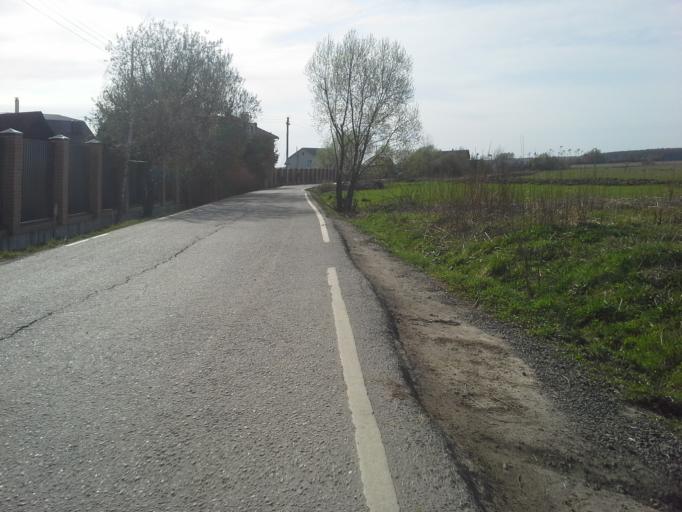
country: RU
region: Moskovskaya
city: Vatutinki
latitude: 55.4603
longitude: 37.3843
